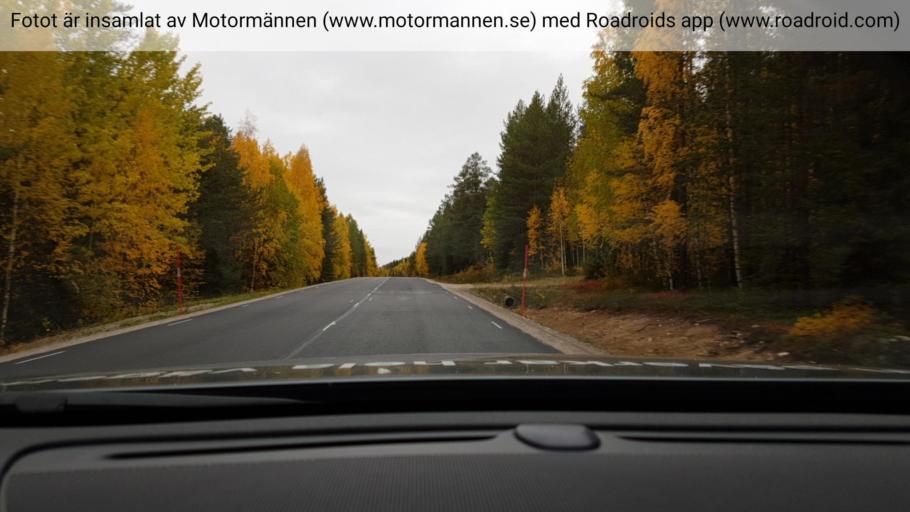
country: SE
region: Norrbotten
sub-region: Overkalix Kommun
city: OEverkalix
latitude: 66.4690
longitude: 22.7924
